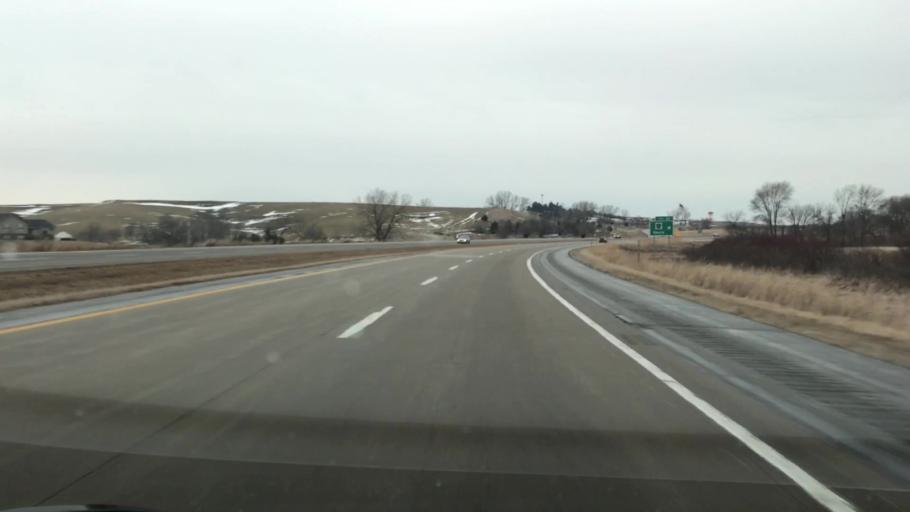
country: US
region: Iowa
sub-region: Pottawattamie County
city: Oakland
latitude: 41.4449
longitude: -95.6054
